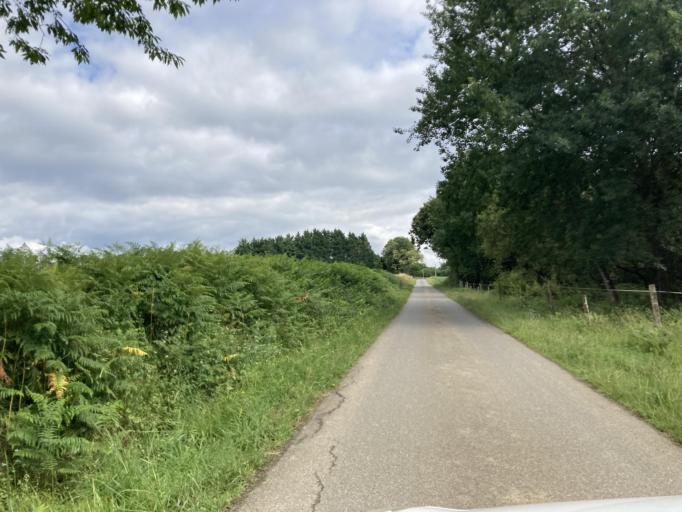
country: FR
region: Aquitaine
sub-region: Departement des Pyrenees-Atlantiques
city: Ledeuix
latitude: 43.2591
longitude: -0.6268
